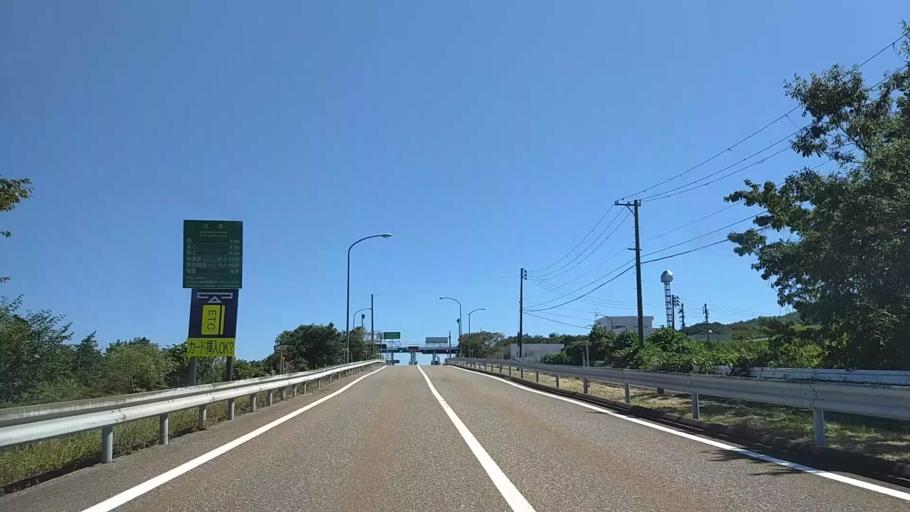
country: JP
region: Niigata
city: Joetsu
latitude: 37.1693
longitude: 138.1094
